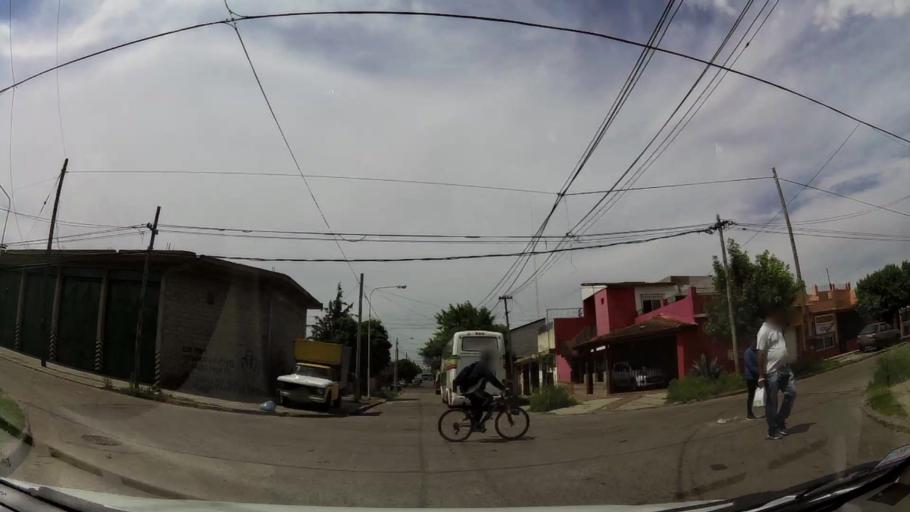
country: AR
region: Buenos Aires
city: San Justo
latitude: -34.6904
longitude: -58.5493
